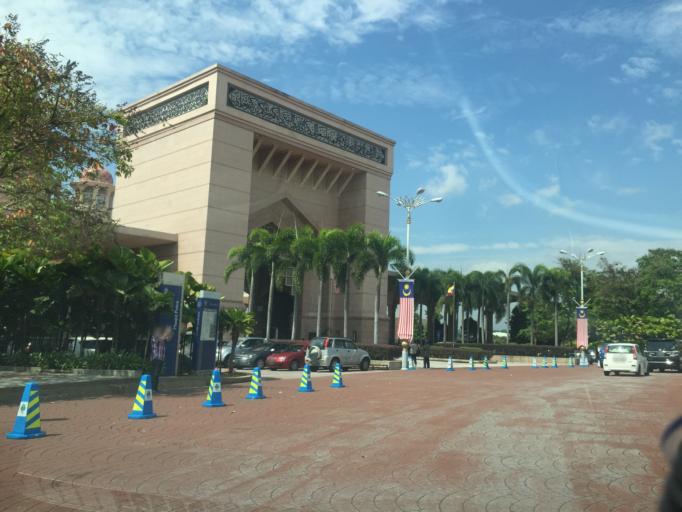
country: MY
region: Putrajaya
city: Putrajaya
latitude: 2.9352
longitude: 101.6903
